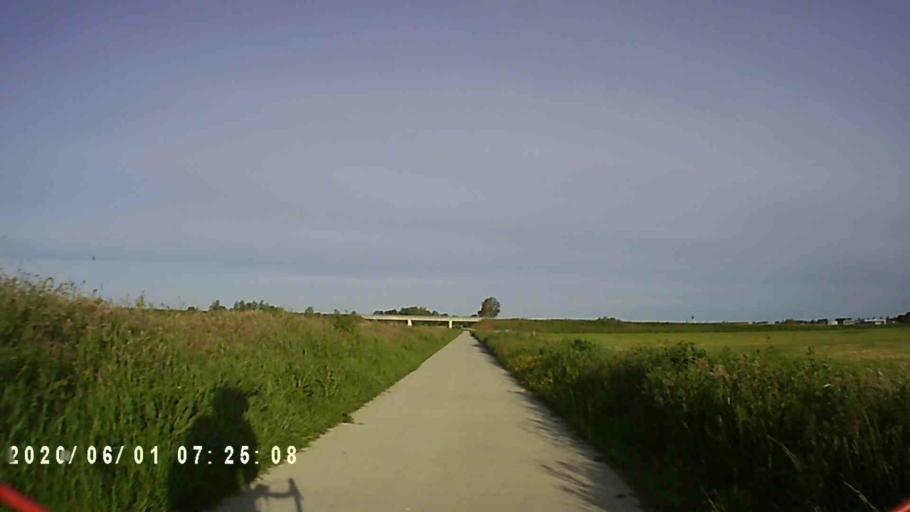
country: NL
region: Friesland
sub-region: Gemeente Dantumadiel
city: Walterswald
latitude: 53.3175
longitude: 6.0259
